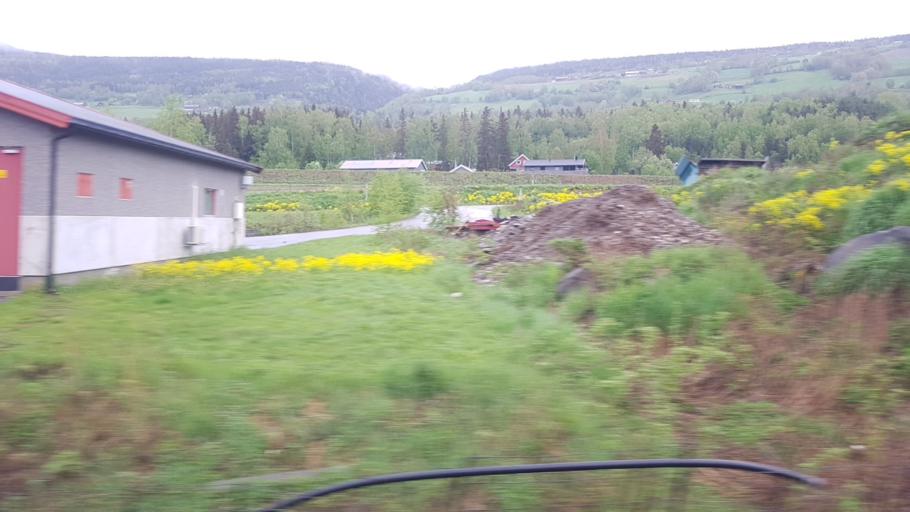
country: NO
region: Oppland
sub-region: Sor-Fron
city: Hundorp
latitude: 61.5628
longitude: 9.9290
